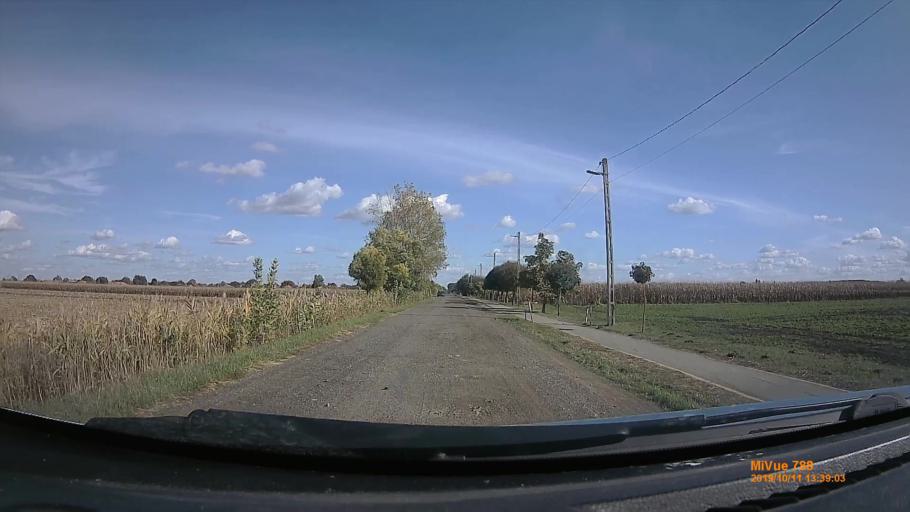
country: HU
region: Hajdu-Bihar
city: Balmazujvaros
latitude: 47.5400
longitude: 21.3291
